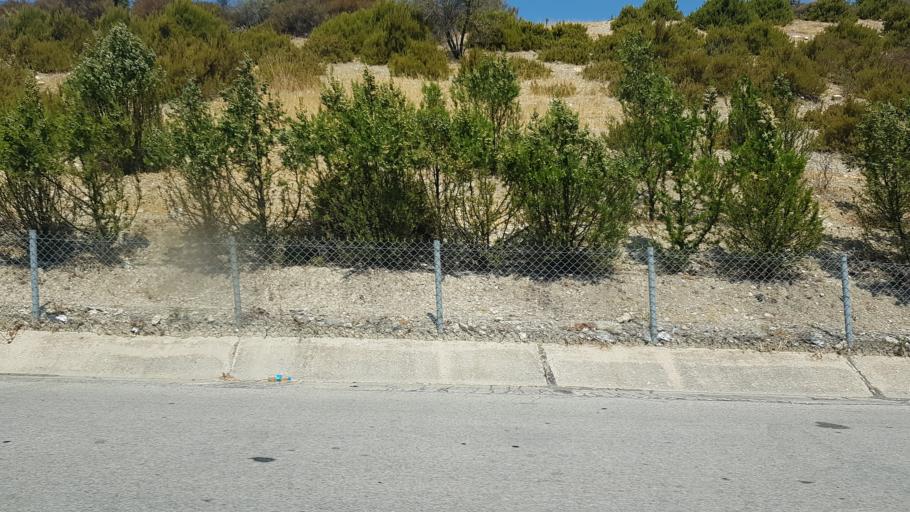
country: TR
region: Izmir
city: Urla
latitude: 38.3214
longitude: 26.7977
